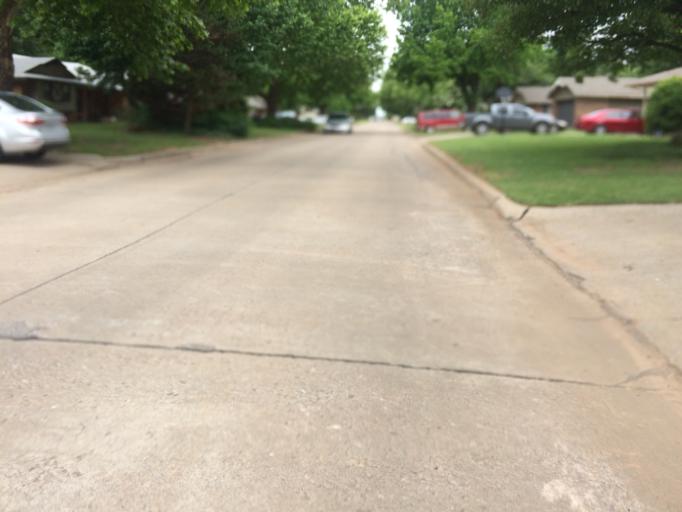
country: US
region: Oklahoma
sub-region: Cleveland County
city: Norman
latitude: 35.2143
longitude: -97.4790
